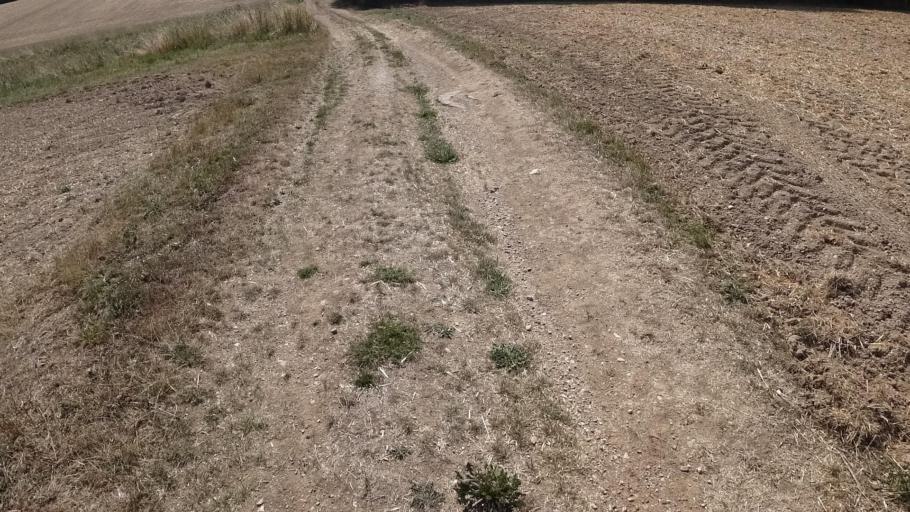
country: DE
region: Rheinland-Pfalz
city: Morschbach
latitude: 50.0275
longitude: 7.6175
